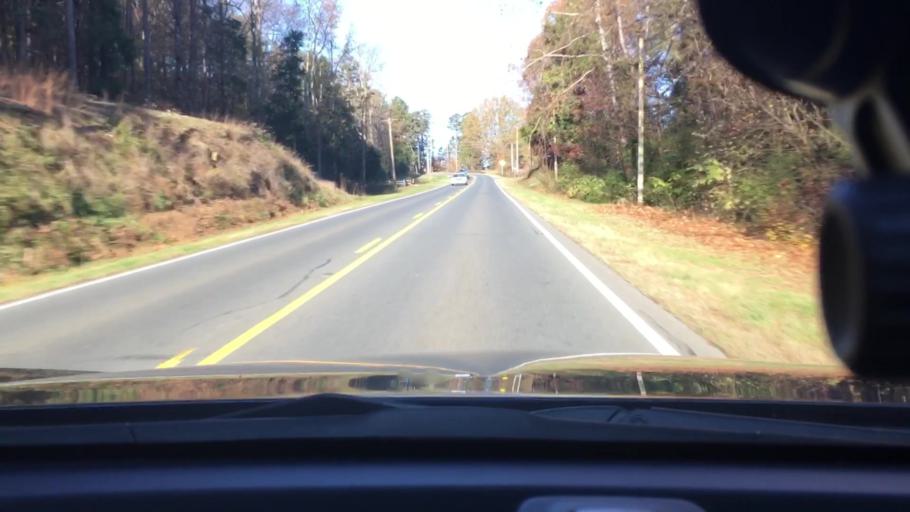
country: US
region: North Carolina
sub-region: Cabarrus County
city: Mount Pleasant
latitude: 35.3849
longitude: -80.3859
